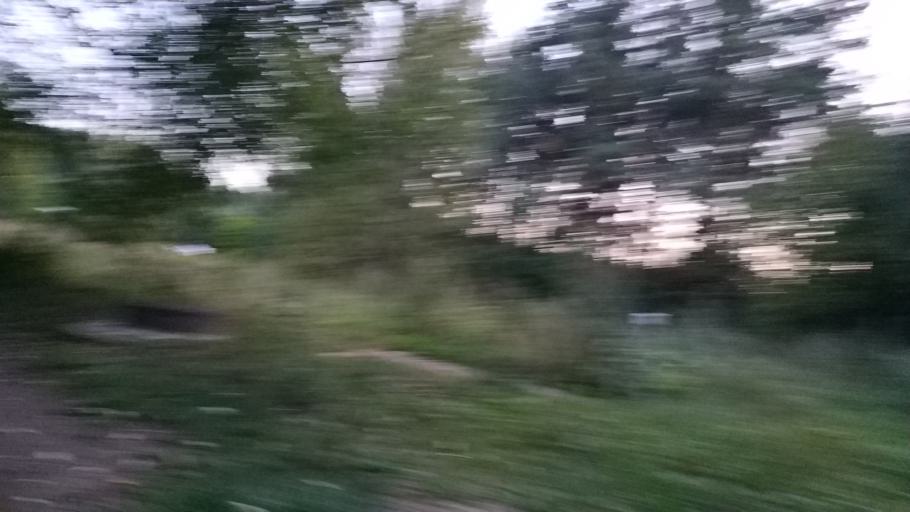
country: RU
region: Moscow
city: Troparevo
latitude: 55.6415
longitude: 37.4694
